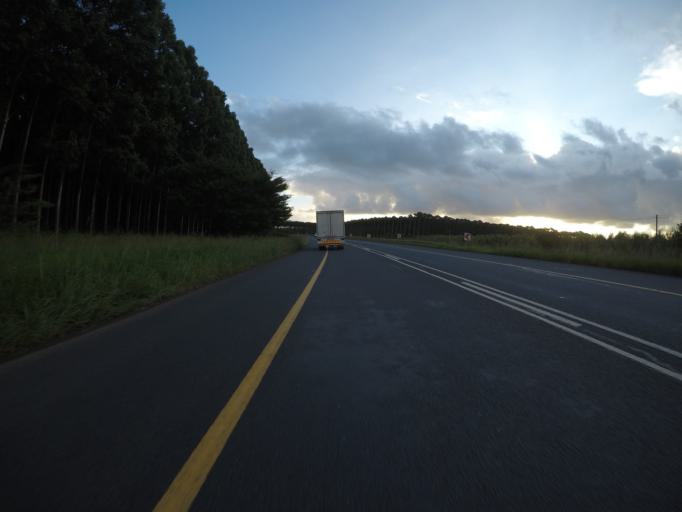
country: ZA
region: KwaZulu-Natal
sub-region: uThungulu District Municipality
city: KwaMbonambi
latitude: -28.5795
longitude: 32.1003
